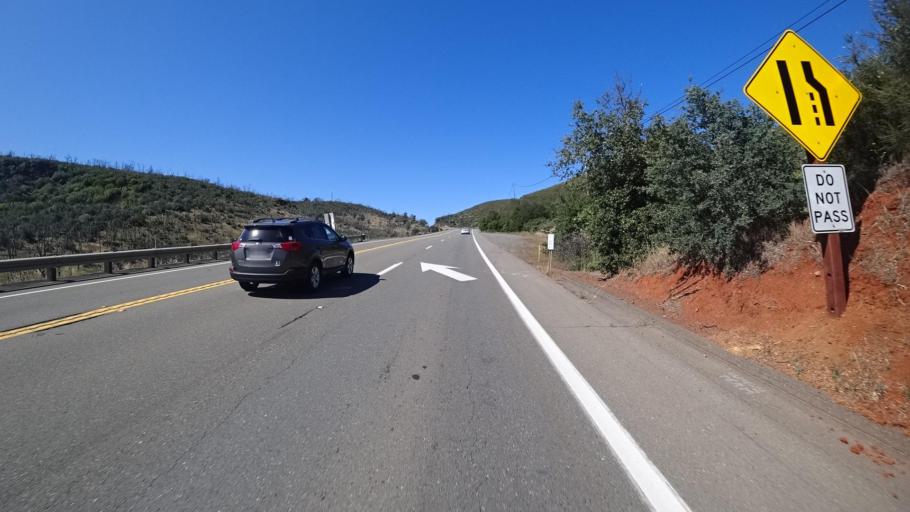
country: US
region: California
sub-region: Lake County
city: Clearlake
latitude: 39.0155
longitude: -122.6010
